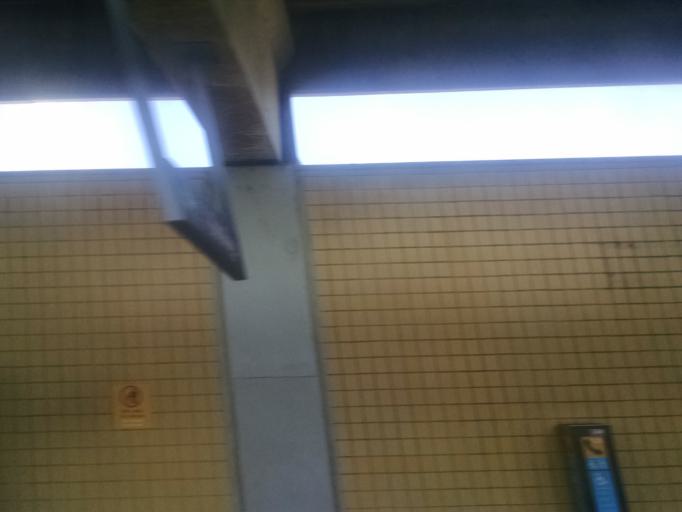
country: BR
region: Rio de Janeiro
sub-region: Duque De Caxias
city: Duque de Caxias
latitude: -22.8628
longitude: -43.3068
